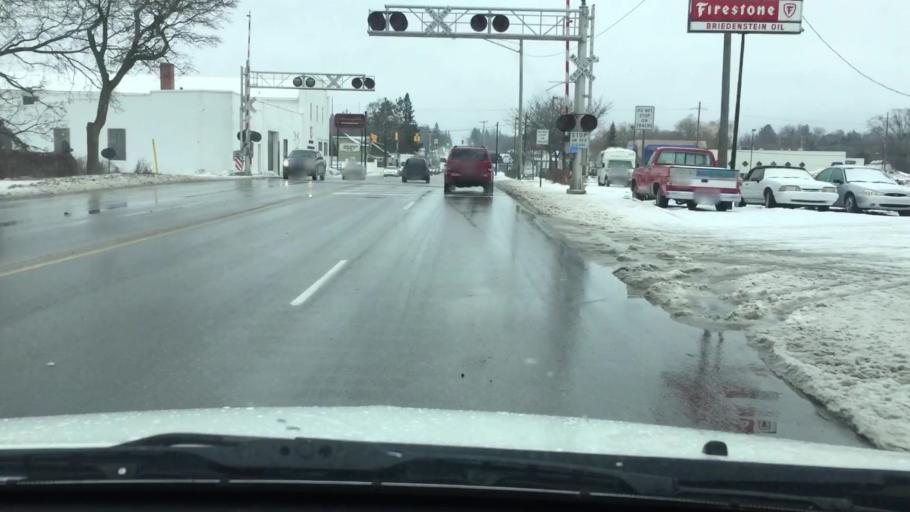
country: US
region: Michigan
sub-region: Wexford County
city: Cadillac
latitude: 44.2464
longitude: -85.3964
